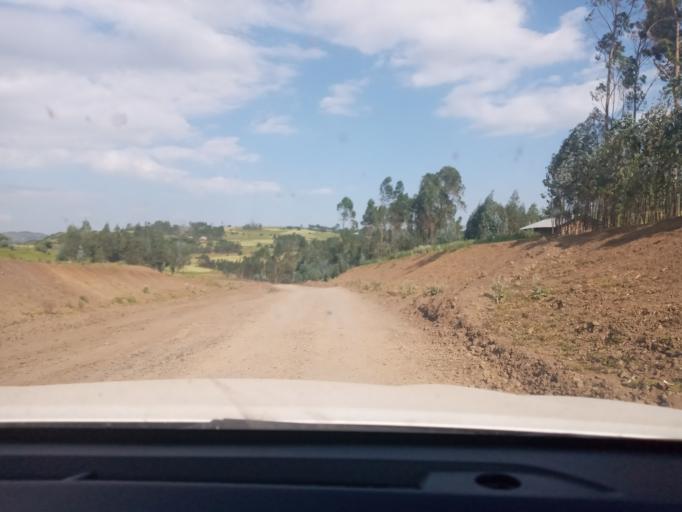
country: ET
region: Amhara
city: Were Ilu
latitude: 10.6140
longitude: 39.0437
